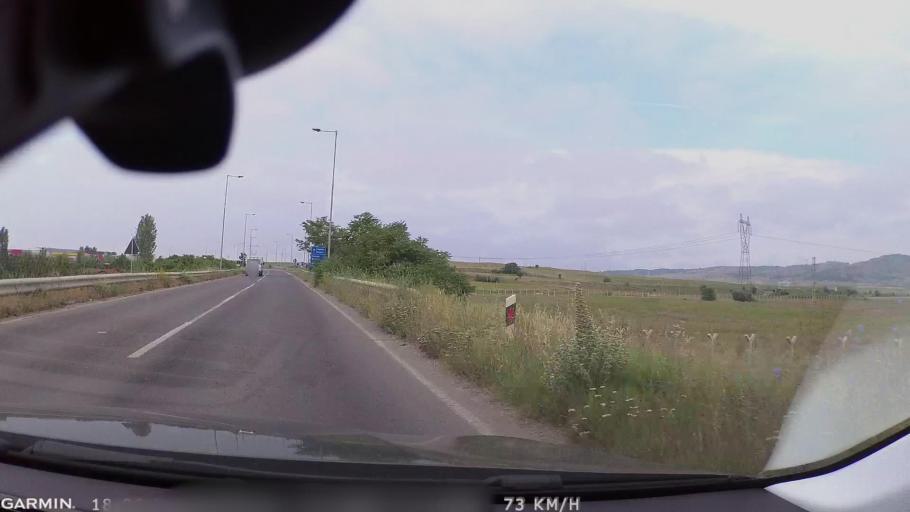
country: MK
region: Stip
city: Shtip
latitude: 41.7656
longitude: 22.1631
